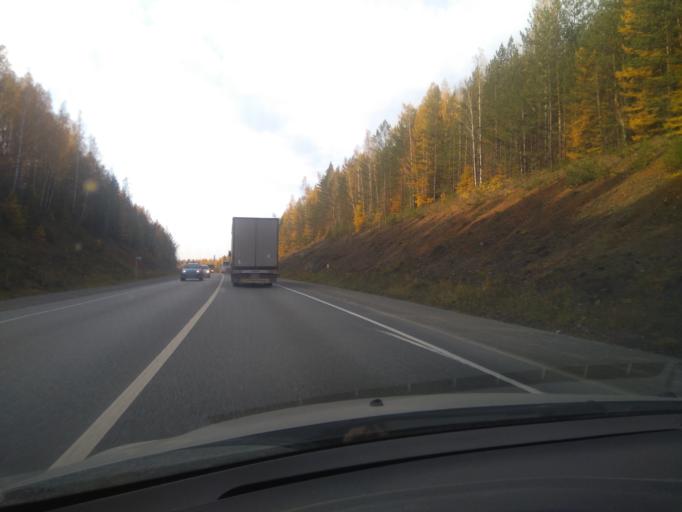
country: RU
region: Sverdlovsk
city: Talitsa
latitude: 56.8404
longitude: 60.0061
